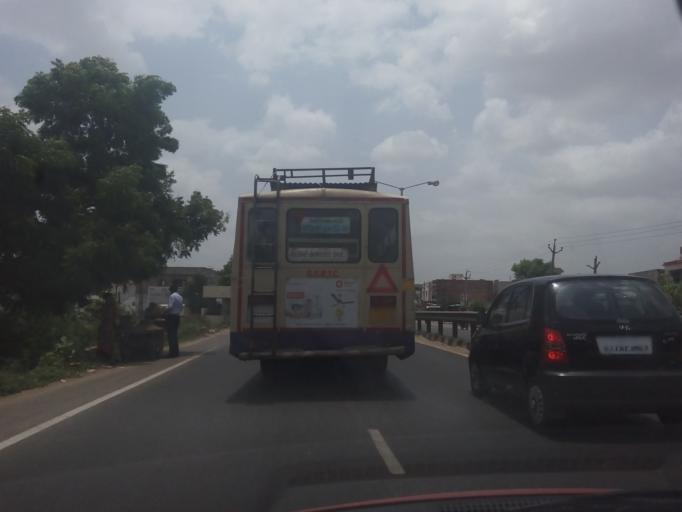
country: IN
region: Gujarat
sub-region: Ahmadabad
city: Sanand
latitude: 22.9868
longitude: 72.3913
